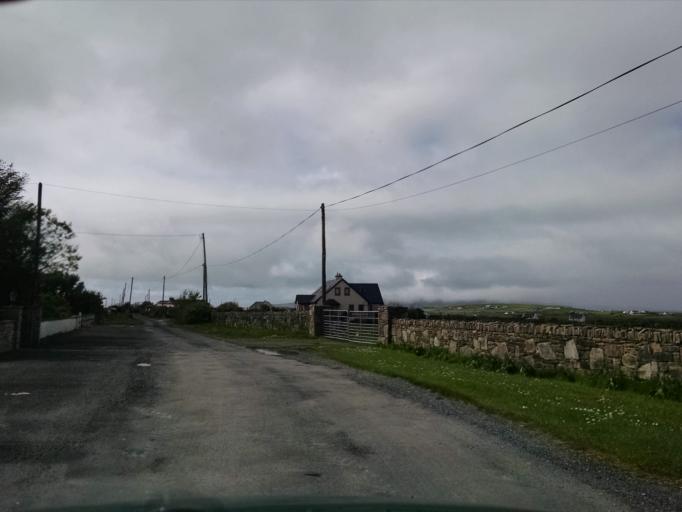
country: IE
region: Connaught
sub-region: County Galway
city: Clifden
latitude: 53.7455
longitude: -9.8665
